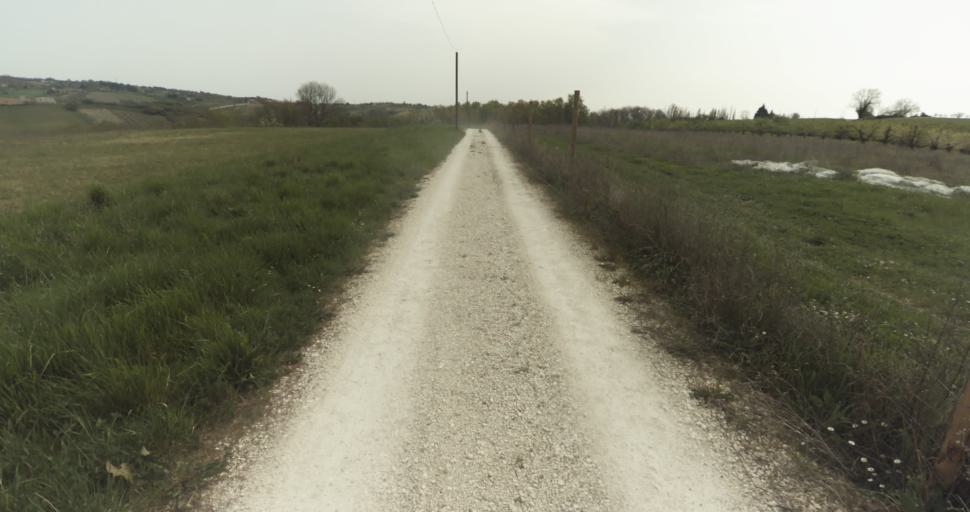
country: FR
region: Midi-Pyrenees
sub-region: Departement du Tarn-et-Garonne
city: Saint-Nicolas-de-la-Grave
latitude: 44.1108
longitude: 1.0433
